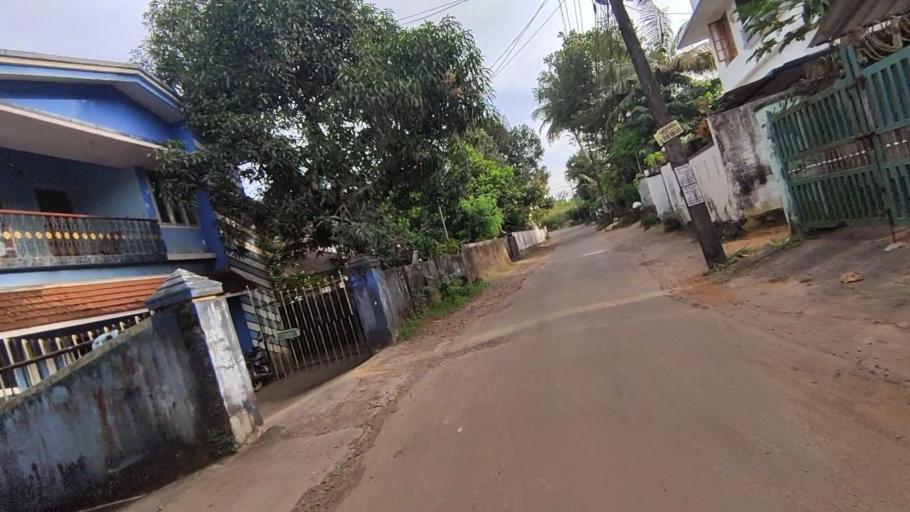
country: IN
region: Kerala
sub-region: Kottayam
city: Kottayam
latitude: 9.6106
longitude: 76.4863
